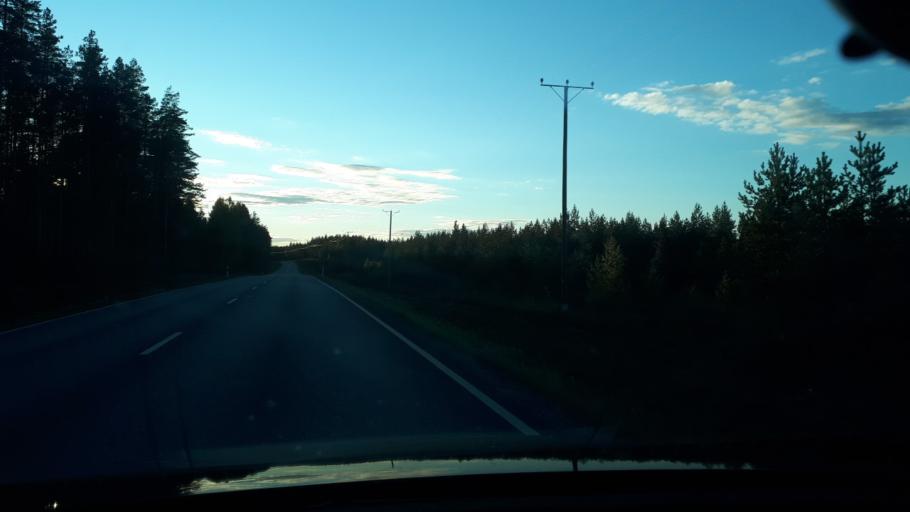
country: FI
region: Northern Ostrobothnia
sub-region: Haapavesi-Siikalatva
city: Pyhaentae
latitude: 64.1387
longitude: 26.2389
